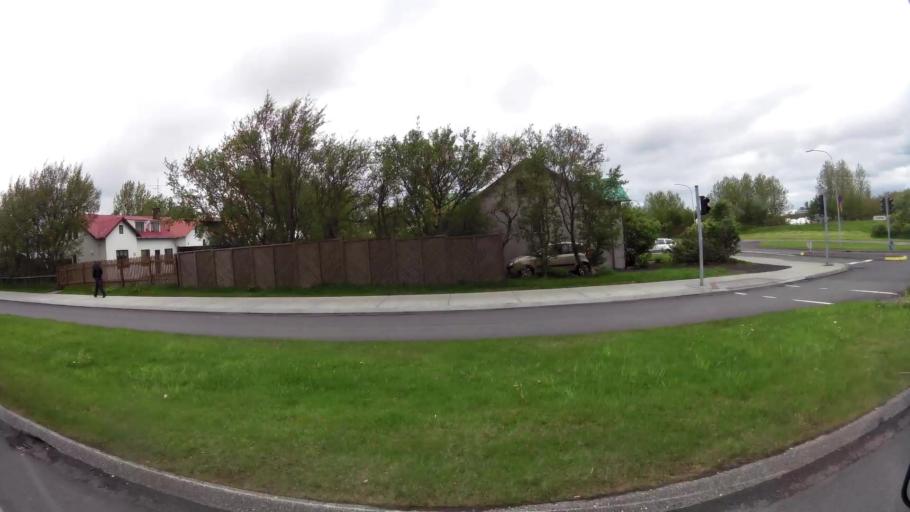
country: IS
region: Capital Region
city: Reykjavik
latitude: 64.1259
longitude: -21.8637
